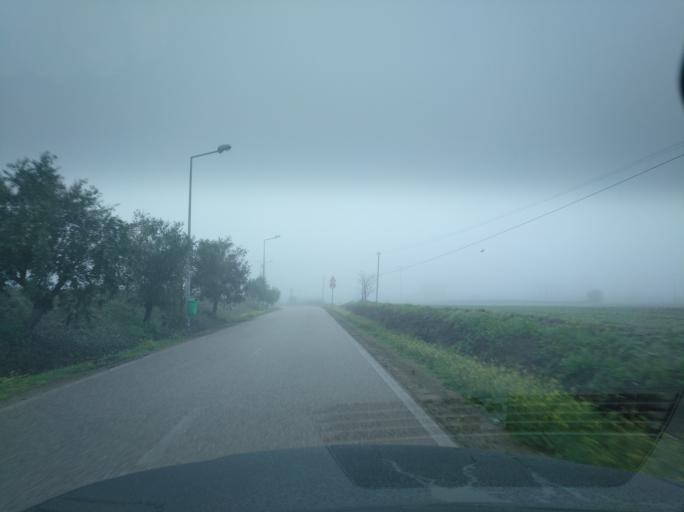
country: PT
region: Portalegre
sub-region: Campo Maior
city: Campo Maior
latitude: 39.0241
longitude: -7.0680
